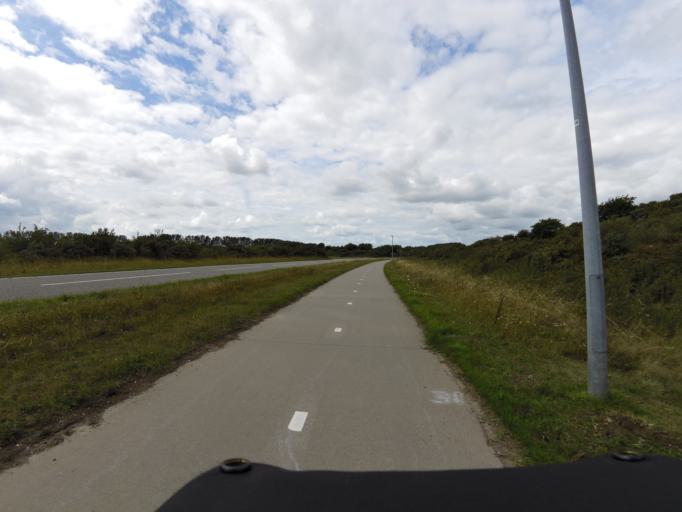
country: NL
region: South Holland
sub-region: Gemeente Goeree-Overflakkee
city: Goedereede
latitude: 51.8287
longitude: 4.0215
